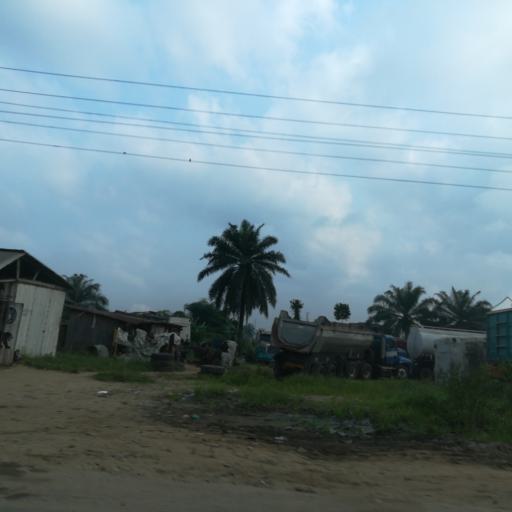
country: NG
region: Rivers
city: Okrika
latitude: 4.7745
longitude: 7.1338
